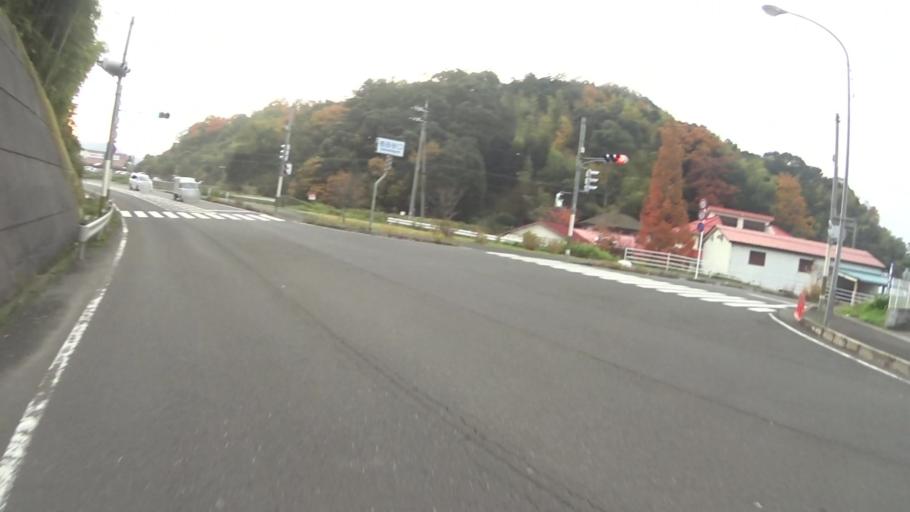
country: JP
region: Kyoto
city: Maizuru
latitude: 35.4632
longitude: 135.4097
